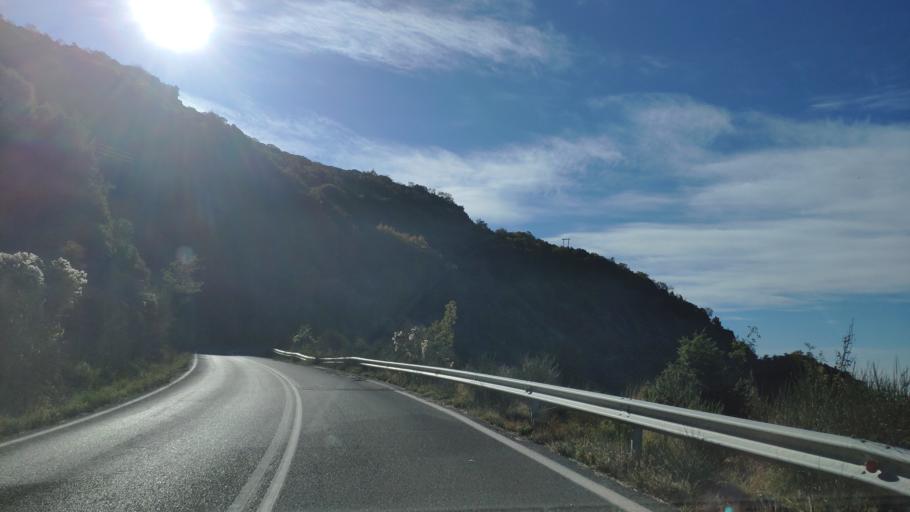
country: GR
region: Peloponnese
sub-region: Nomos Arkadias
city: Dimitsana
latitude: 37.5642
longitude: 22.0622
